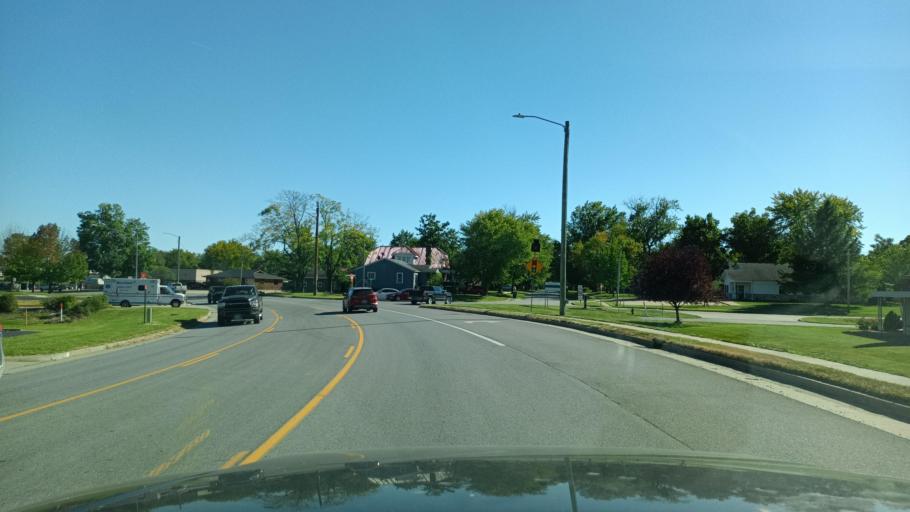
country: US
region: Missouri
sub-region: Macon County
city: Macon
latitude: 39.7475
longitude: -92.4681
